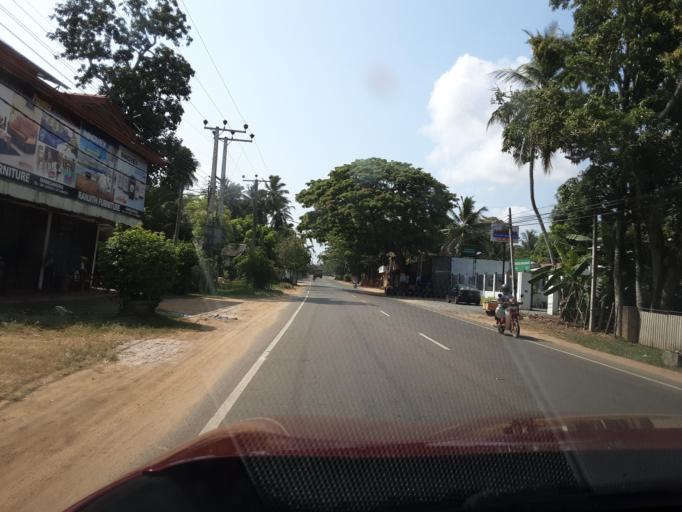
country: LK
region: Southern
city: Tangalla
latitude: 6.3049
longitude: 81.2341
